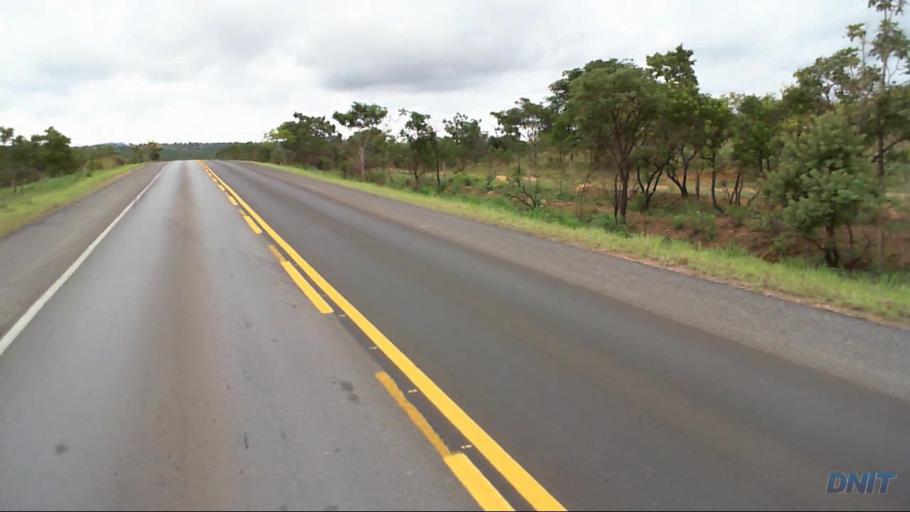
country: BR
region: Goias
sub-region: Padre Bernardo
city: Padre Bernardo
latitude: -15.2133
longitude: -48.5761
